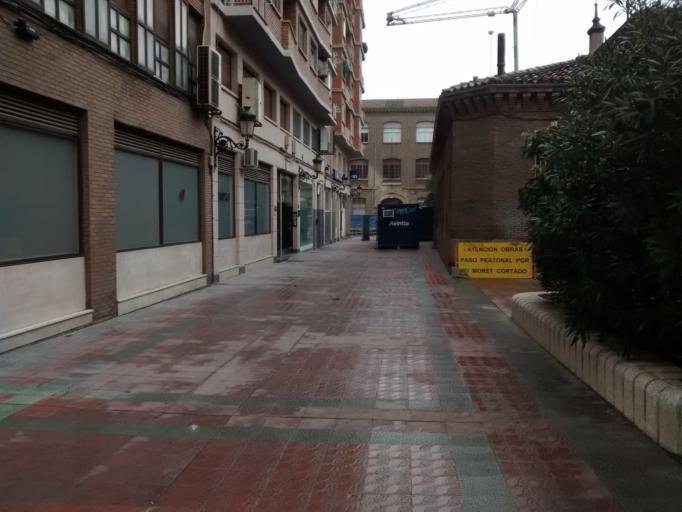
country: ES
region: Aragon
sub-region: Provincia de Zaragoza
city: Zaragoza
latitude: 41.6491
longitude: -0.8775
